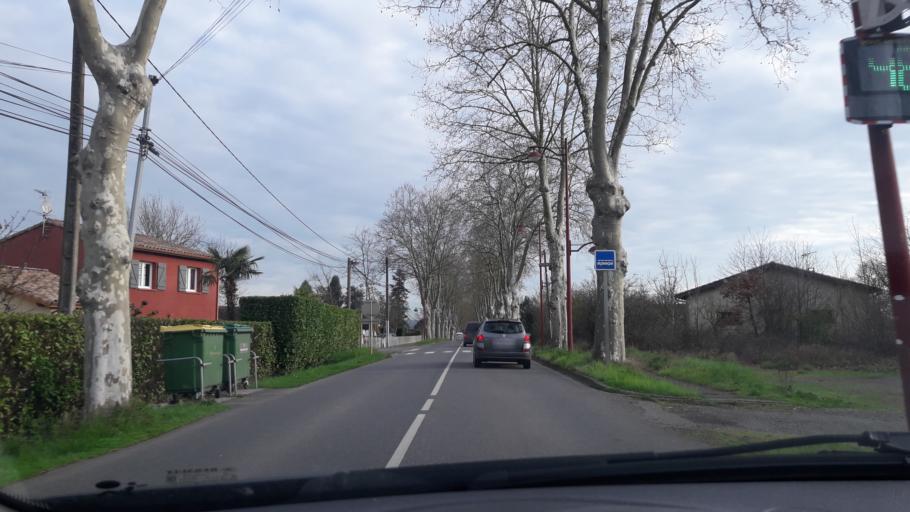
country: FR
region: Midi-Pyrenees
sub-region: Departement de la Haute-Garonne
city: Grenade
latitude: 43.7632
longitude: 1.2923
